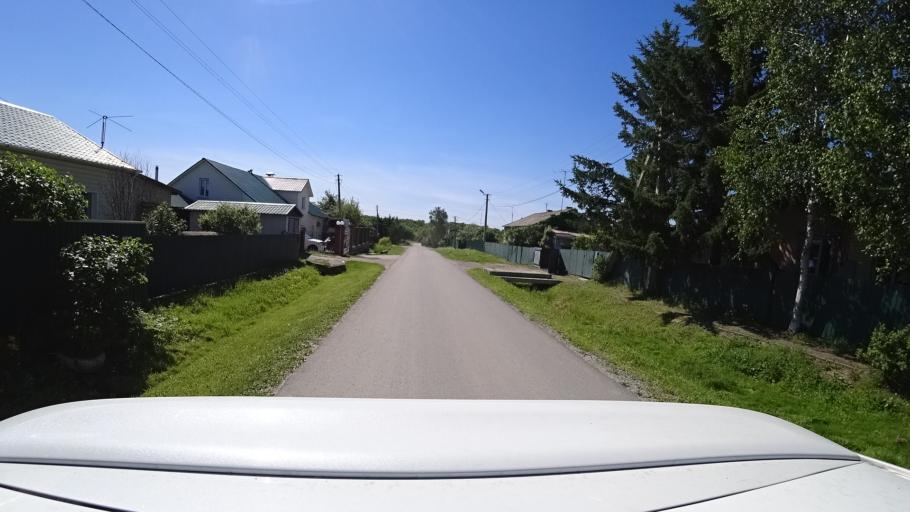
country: RU
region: Khabarovsk Krai
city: Topolevo
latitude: 48.5568
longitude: 135.1891
